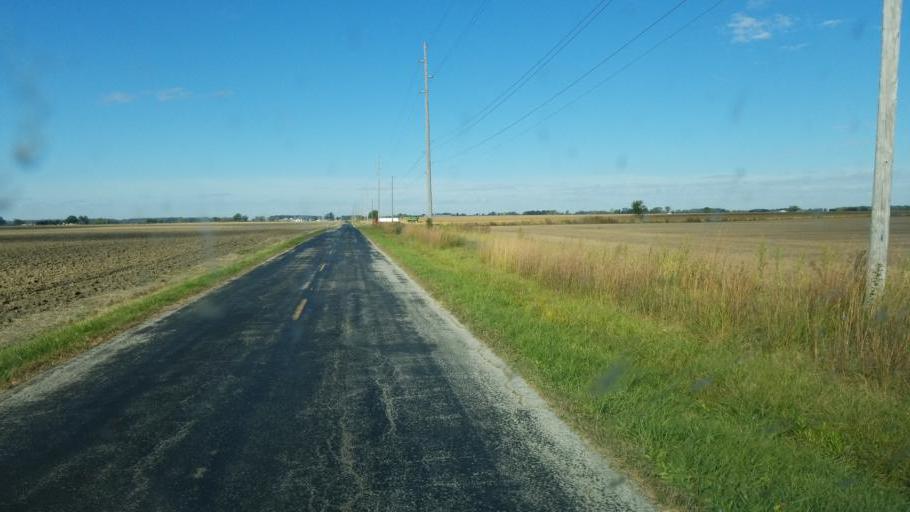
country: US
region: Ohio
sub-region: Marion County
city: Marion
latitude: 40.6884
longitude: -83.0945
